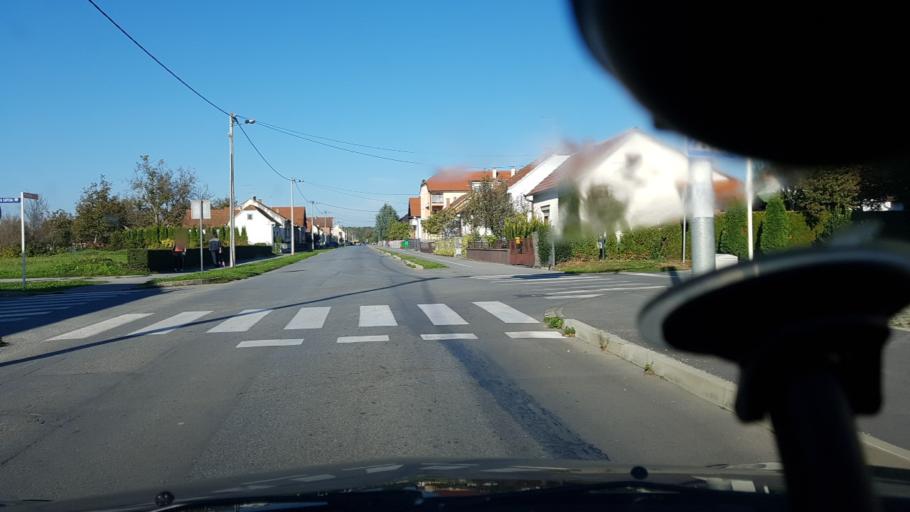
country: HR
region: Bjelovarsko-Bilogorska
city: Bjelovar
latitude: 45.9165
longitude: 16.8581
